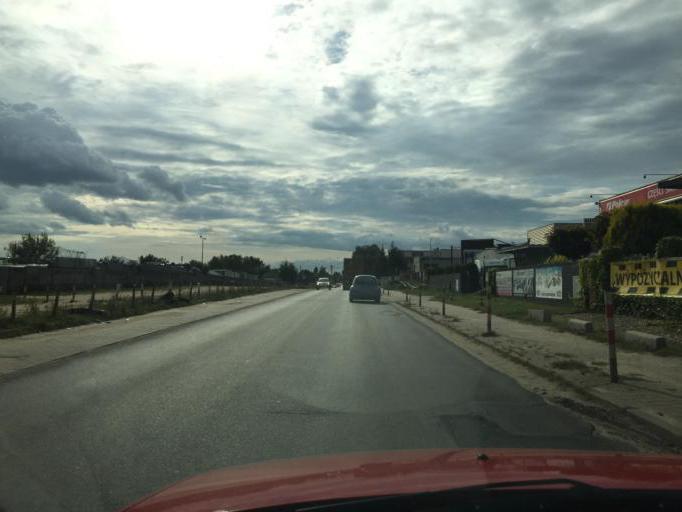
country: PL
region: Greater Poland Voivodeship
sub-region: Powiat poznanski
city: Baranowo
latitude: 52.4205
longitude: 16.7967
